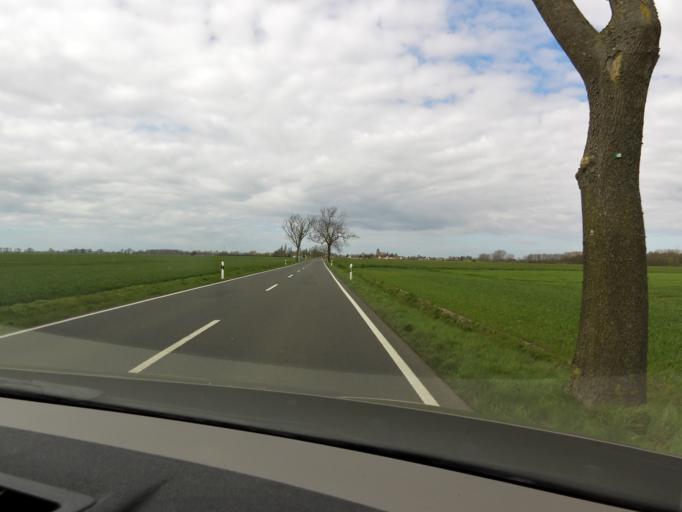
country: DE
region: Mecklenburg-Vorpommern
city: Gingst
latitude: 54.4404
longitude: 13.2673
